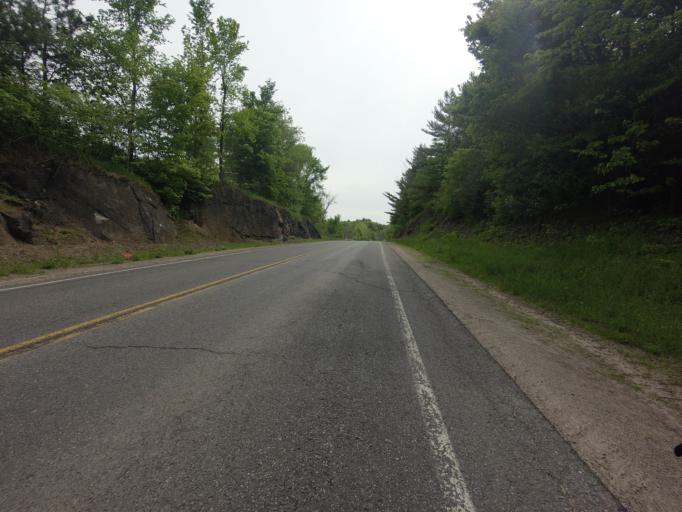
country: US
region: New York
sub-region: St. Lawrence County
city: Gouverneur
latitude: 44.3363
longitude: -75.2380
